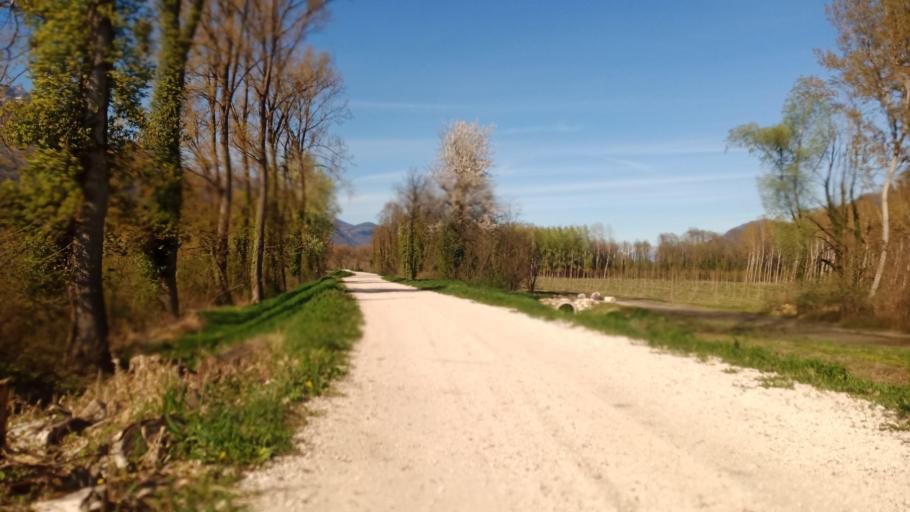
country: FR
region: Rhone-Alpes
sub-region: Departement de l'Isere
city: Le Champ-pres-Froges
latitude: 45.2960
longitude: 5.9327
